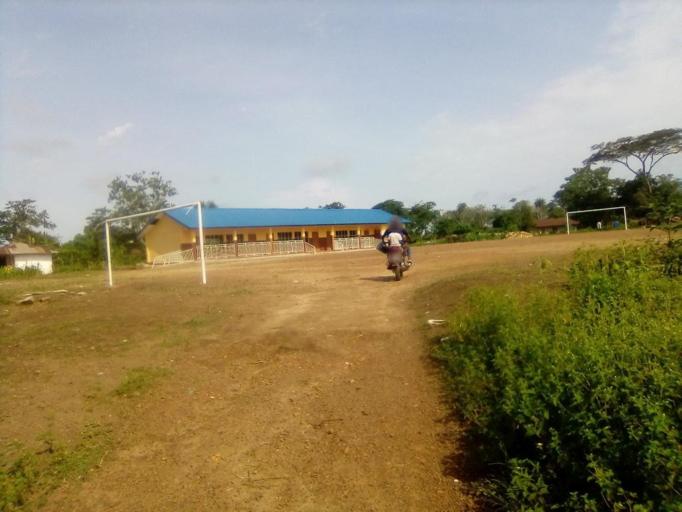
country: SL
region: Southern Province
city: Pujehun
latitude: 7.3640
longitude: -11.7271
